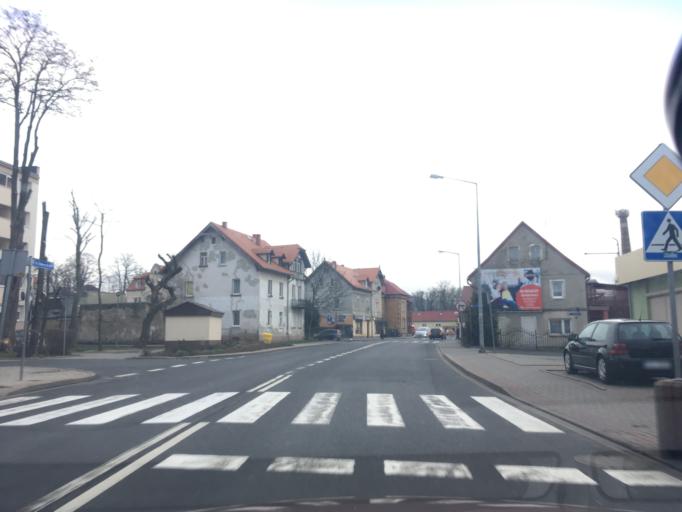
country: PL
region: Lower Silesian Voivodeship
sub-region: Powiat zgorzelecki
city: Bogatynia
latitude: 50.9029
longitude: 14.9611
